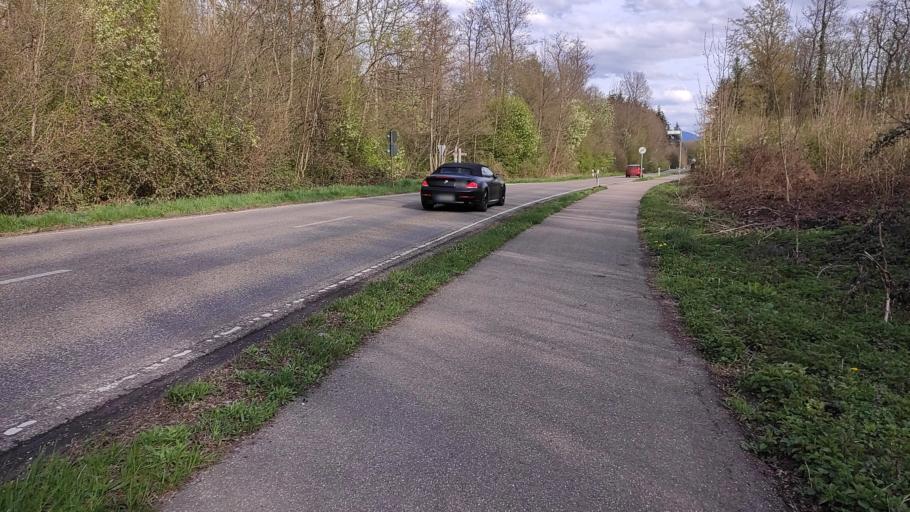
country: DE
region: Baden-Wuerttemberg
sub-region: Freiburg Region
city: Umkirch
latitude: 47.9971
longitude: 7.7683
